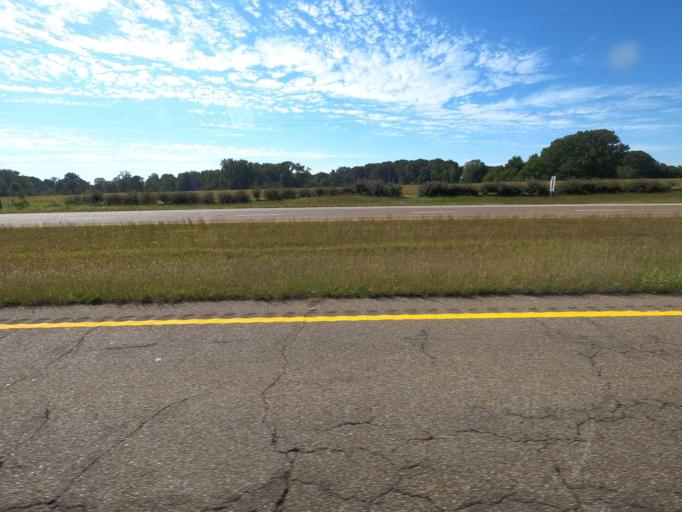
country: US
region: Tennessee
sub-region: Crockett County
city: Alamo
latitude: 35.7482
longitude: -89.1039
